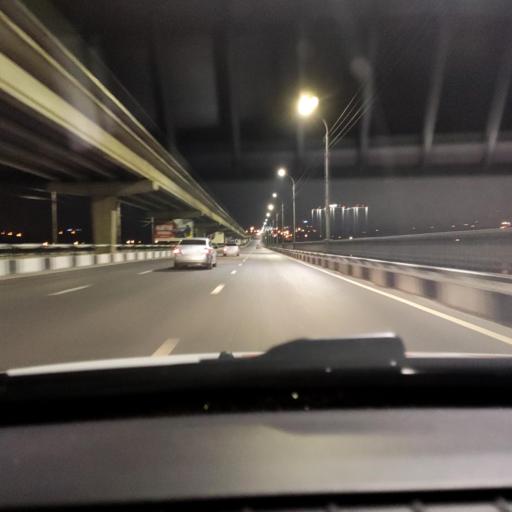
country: RU
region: Voronezj
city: Voronezh
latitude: 51.6916
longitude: 39.2426
